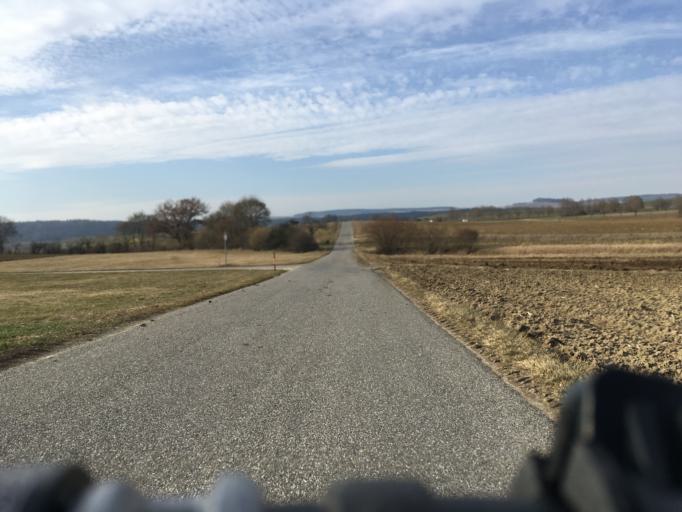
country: CH
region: Schaffhausen
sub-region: Bezirk Reiat
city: Thayngen
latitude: 47.7820
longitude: 8.7069
